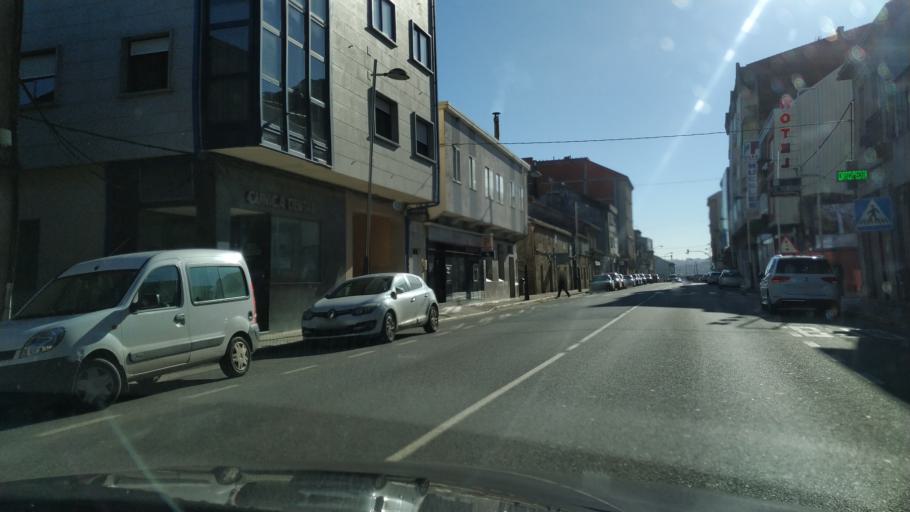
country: ES
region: Galicia
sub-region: Provincia de Pontevedra
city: Silleda
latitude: 42.7301
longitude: -8.3043
